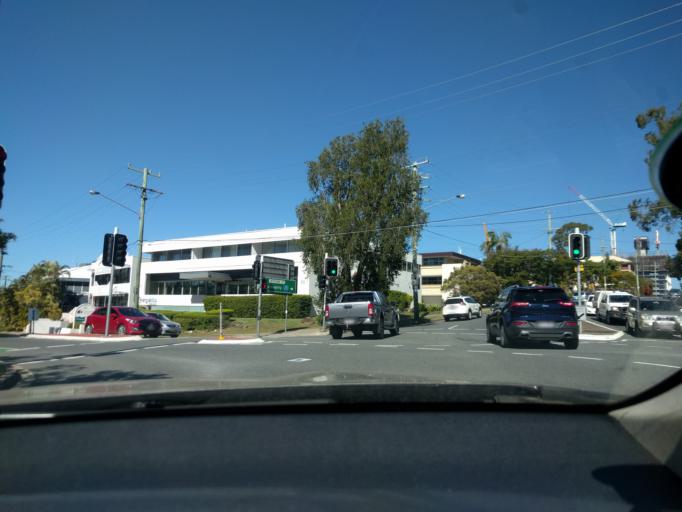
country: AU
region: Queensland
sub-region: Brisbane
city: Toowong
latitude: -27.4807
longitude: 152.9913
